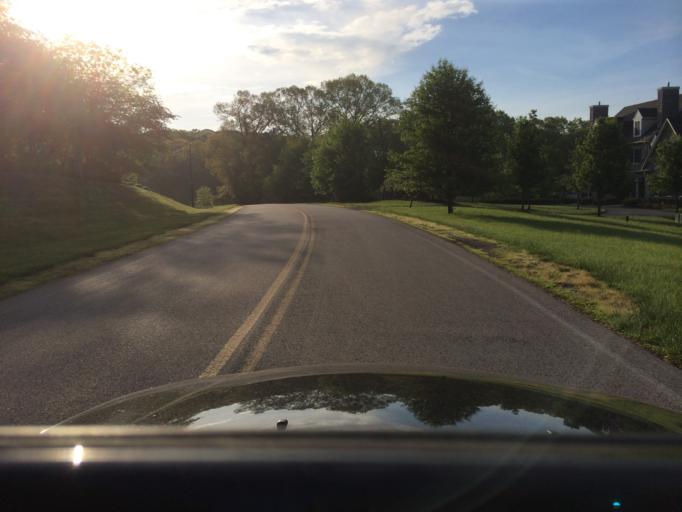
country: US
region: Maryland
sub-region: Howard County
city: Highland
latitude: 39.2167
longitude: -76.9861
